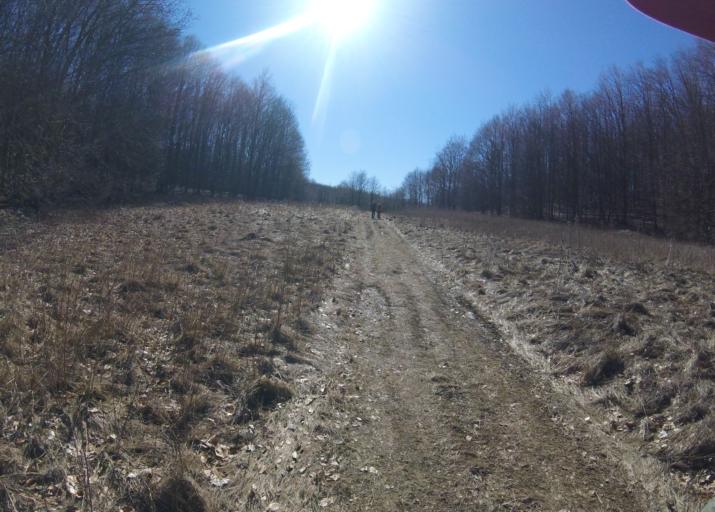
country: HU
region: Heves
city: Szilvasvarad
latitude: 48.0632
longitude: 20.4701
